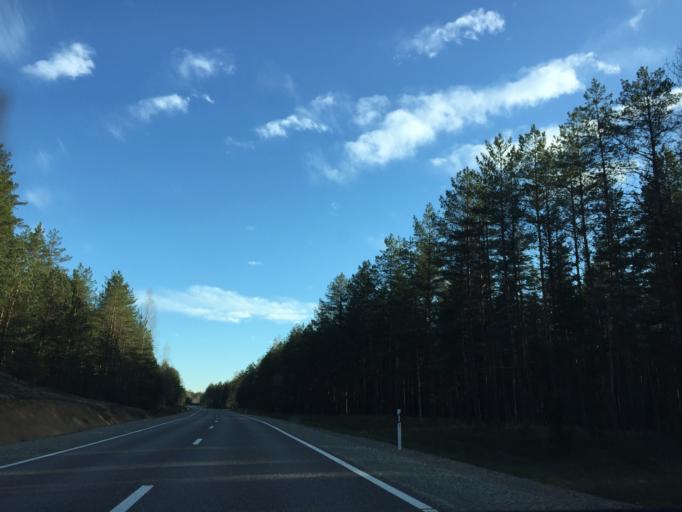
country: LV
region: Strenci
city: Seda
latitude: 57.6674
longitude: 25.8759
